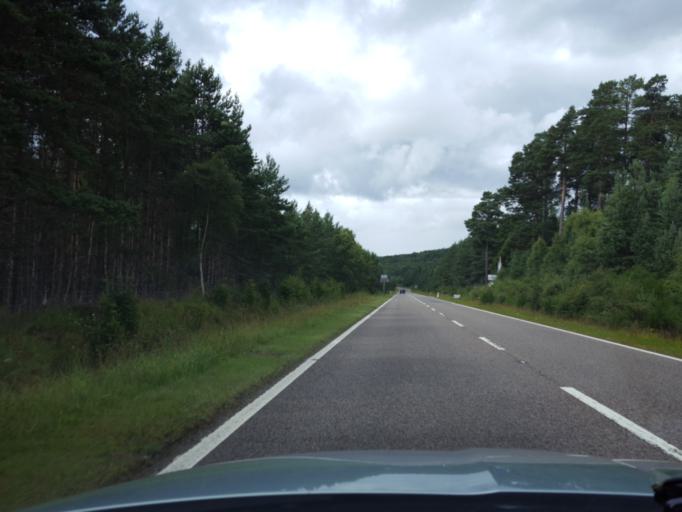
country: GB
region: Scotland
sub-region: Highland
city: Grantown on Spey
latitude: 57.2819
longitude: -3.6937
